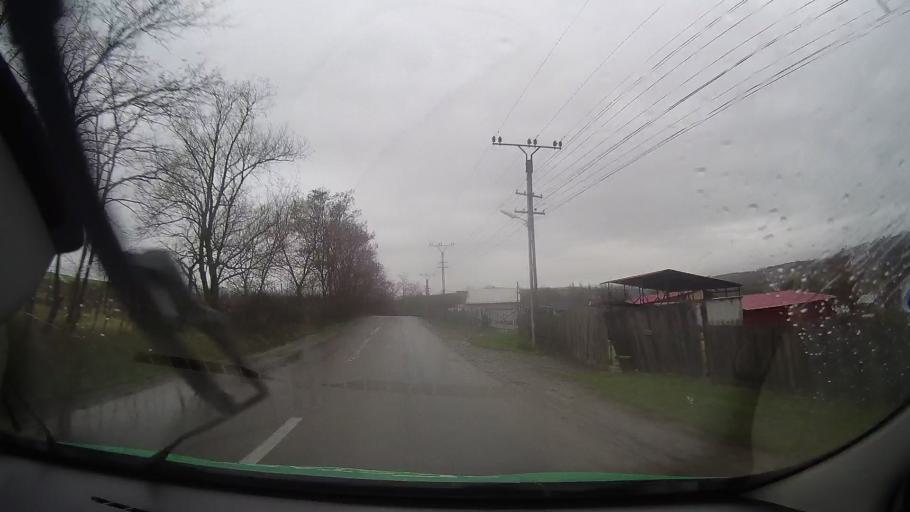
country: RO
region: Mures
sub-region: Comuna Brancovenesti
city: Valenii de Mures
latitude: 46.9239
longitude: 24.7722
